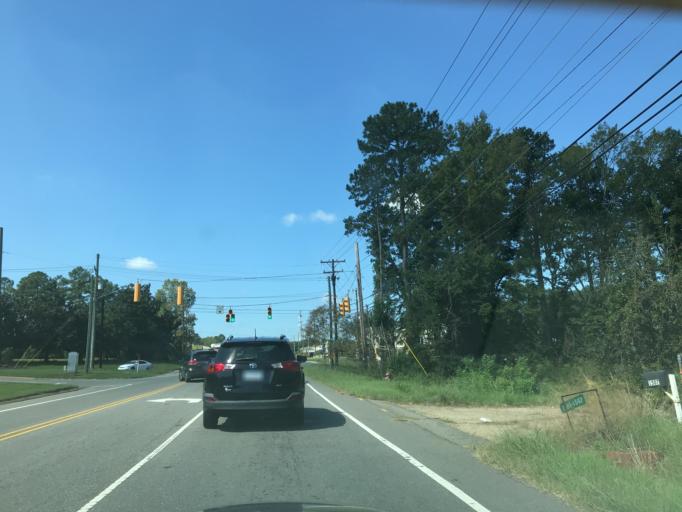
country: US
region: North Carolina
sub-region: Durham County
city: Durham
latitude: 35.9037
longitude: -78.9109
